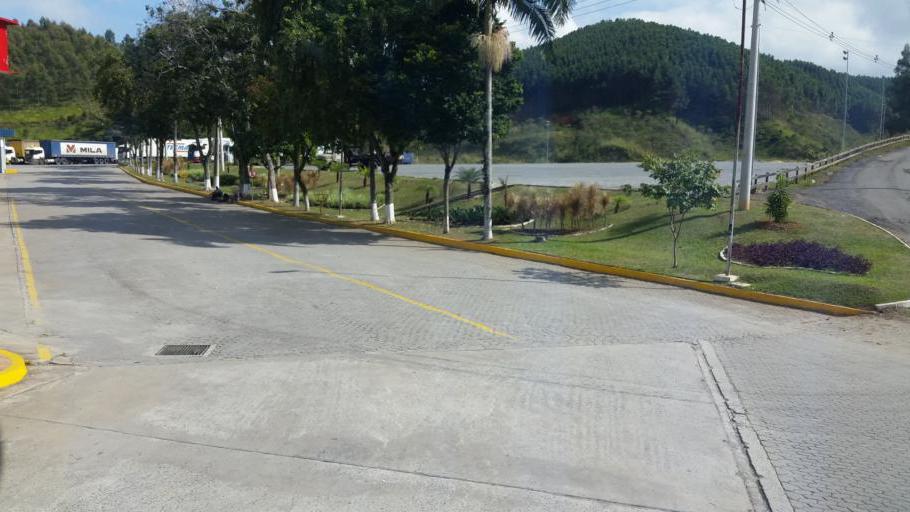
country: BR
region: Rio de Janeiro
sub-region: Itatiaia
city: Itatiaia
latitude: -22.5291
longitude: -44.7507
